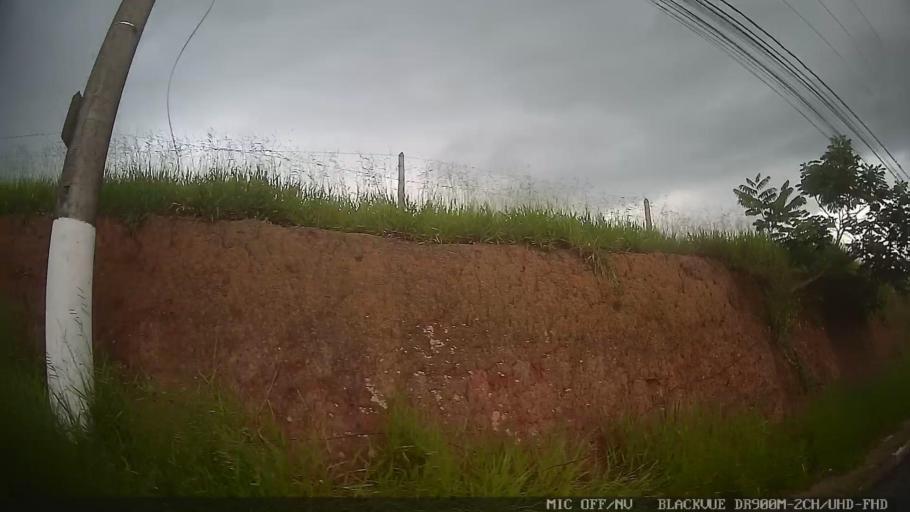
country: BR
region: Sao Paulo
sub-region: Atibaia
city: Atibaia
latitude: -23.1471
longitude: -46.5899
